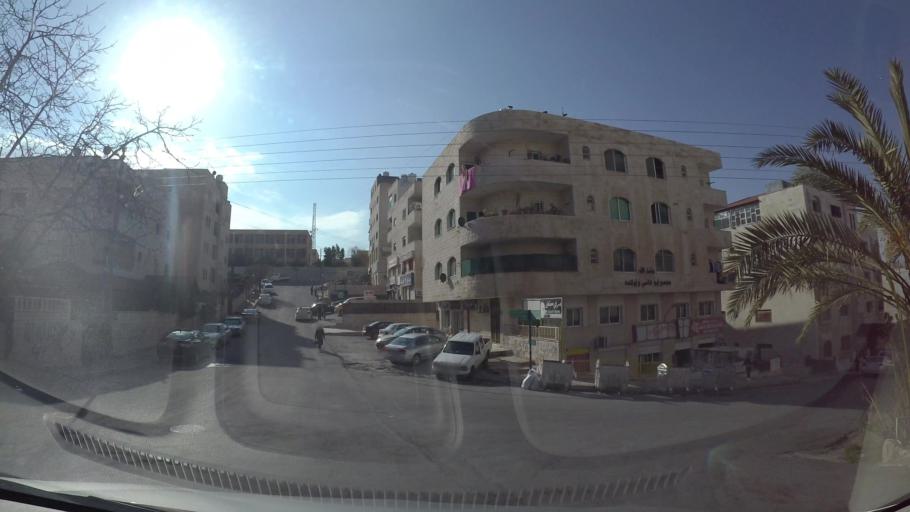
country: JO
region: Amman
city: Al Jubayhah
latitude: 32.0208
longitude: 35.8515
